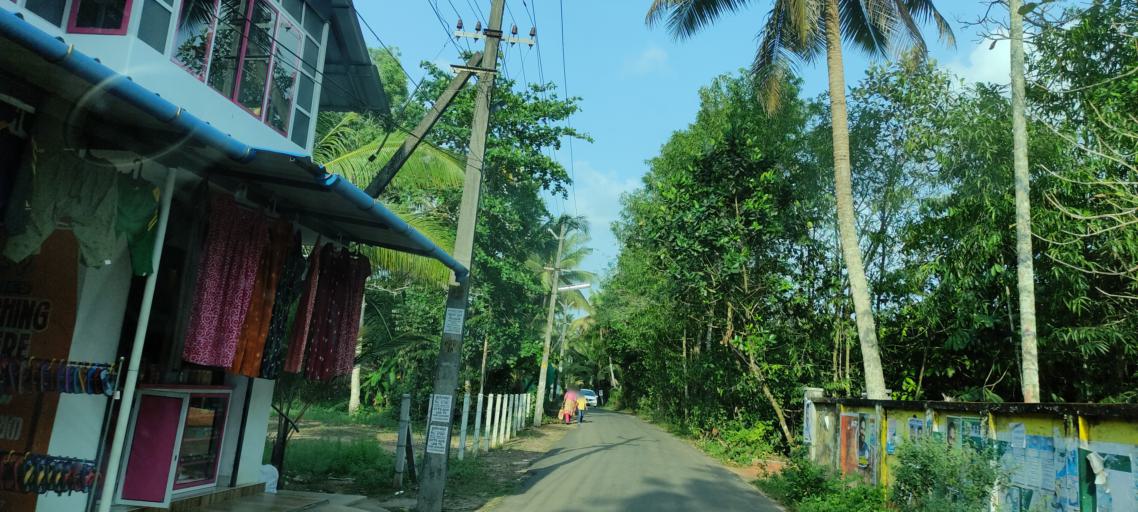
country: IN
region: Kerala
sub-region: Alappuzha
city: Vayalar
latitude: 9.7281
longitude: 76.3014
